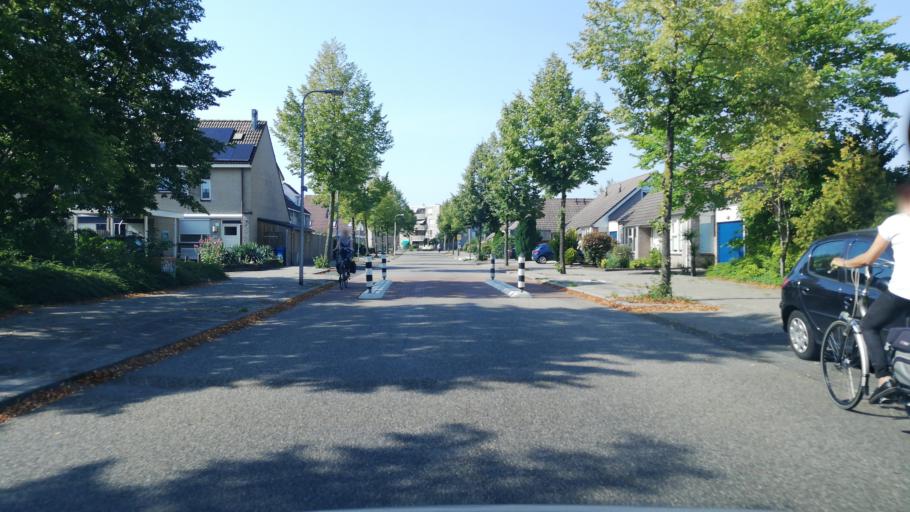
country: NL
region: Overijssel
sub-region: Gemeente Zwolle
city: Zwolle
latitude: 52.4949
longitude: 6.0969
